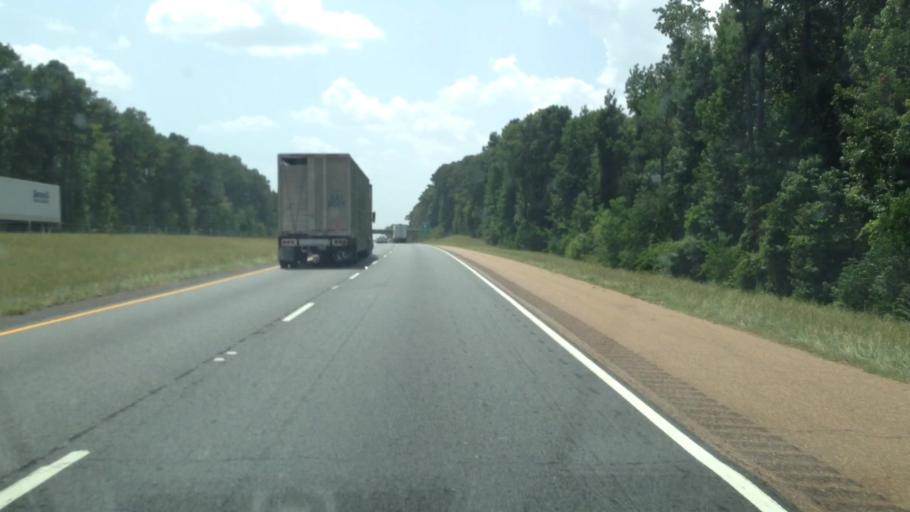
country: US
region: Louisiana
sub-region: Bienville Parish
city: Arcadia
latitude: 32.5673
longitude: -92.9308
